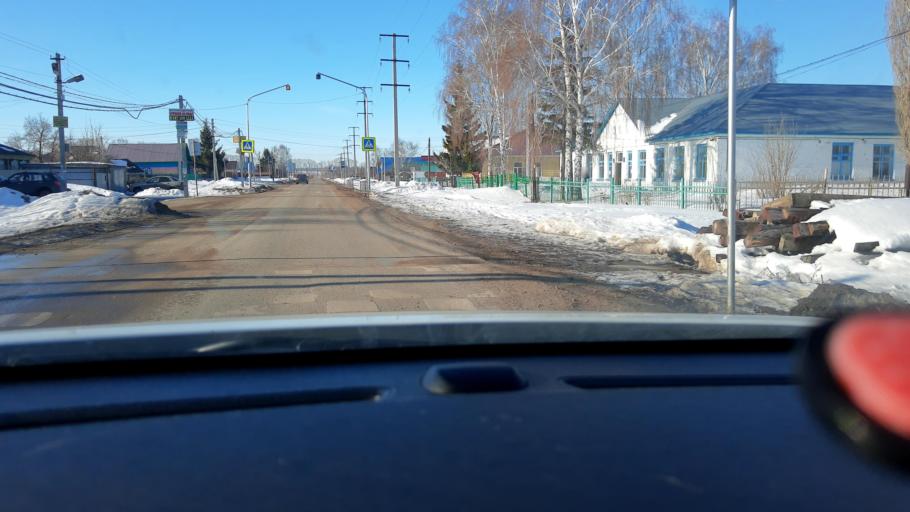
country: RU
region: Bashkortostan
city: Kabakovo
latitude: 54.5181
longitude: 55.9468
